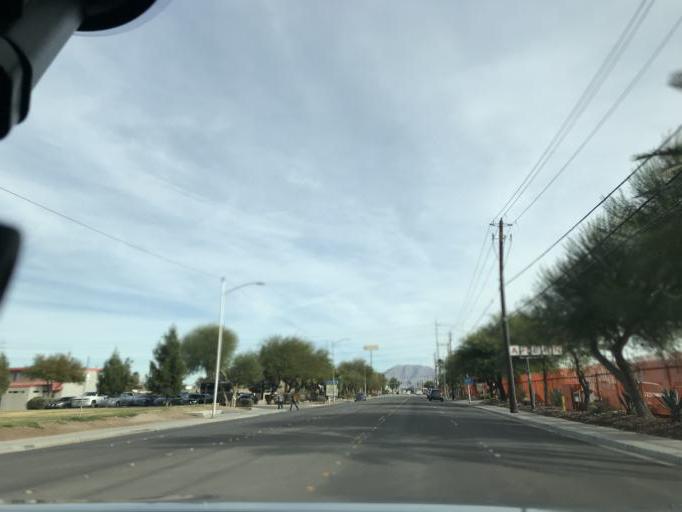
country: US
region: Nevada
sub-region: Clark County
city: Las Vegas
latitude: 36.1771
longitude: -115.1650
